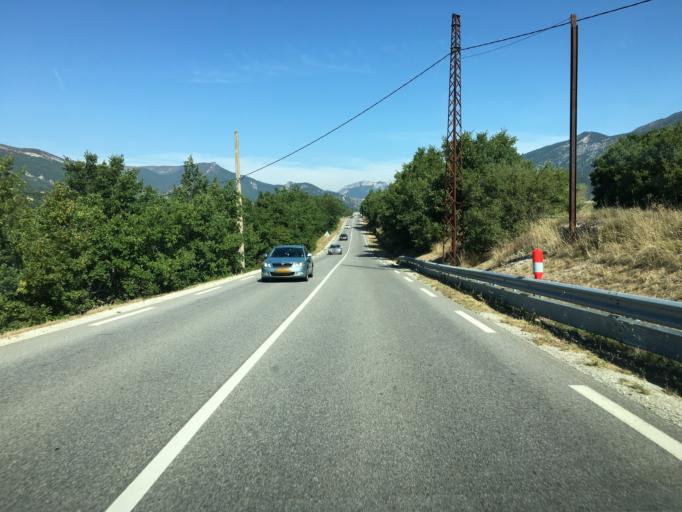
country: FR
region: Provence-Alpes-Cote d'Azur
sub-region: Departement des Hautes-Alpes
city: Serres
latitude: 44.3878
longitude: 5.7432
